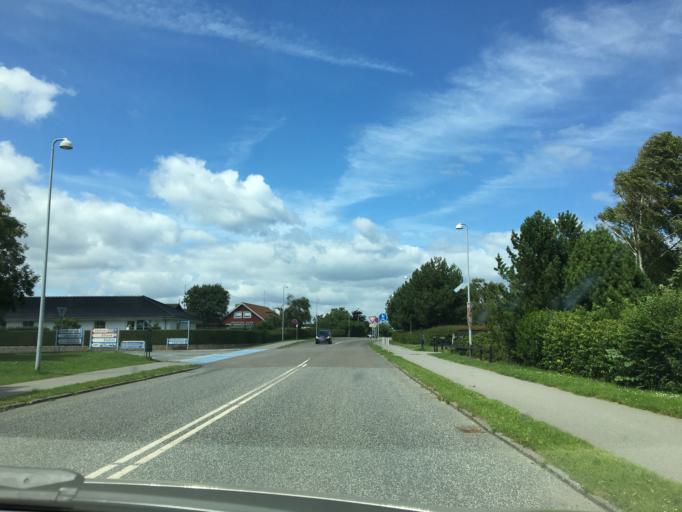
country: DK
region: South Denmark
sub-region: Langeland Kommune
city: Rudkobing
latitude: 54.9418
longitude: 10.7216
